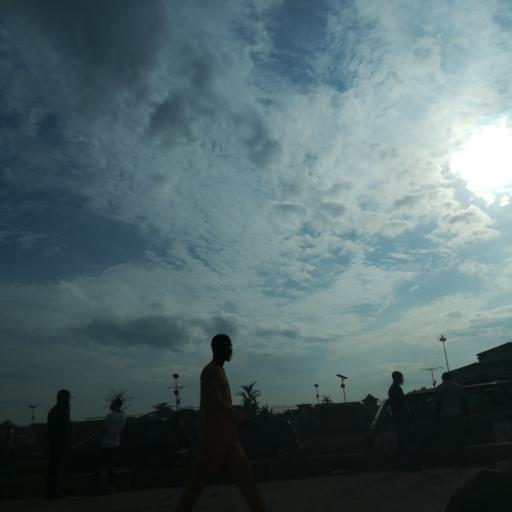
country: NG
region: Lagos
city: Oshodi
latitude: 6.5628
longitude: 3.3488
